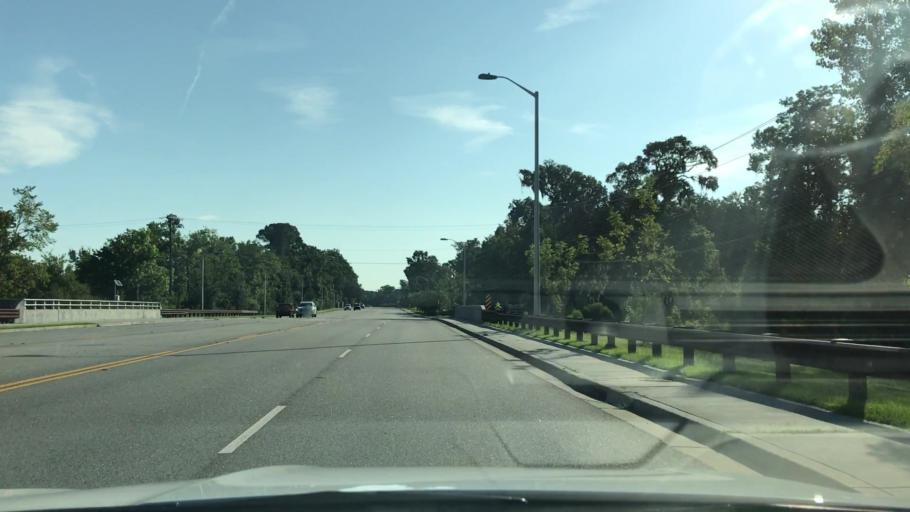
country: US
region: South Carolina
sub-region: Charleston County
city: Shell Point
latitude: 32.8296
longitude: -80.0751
